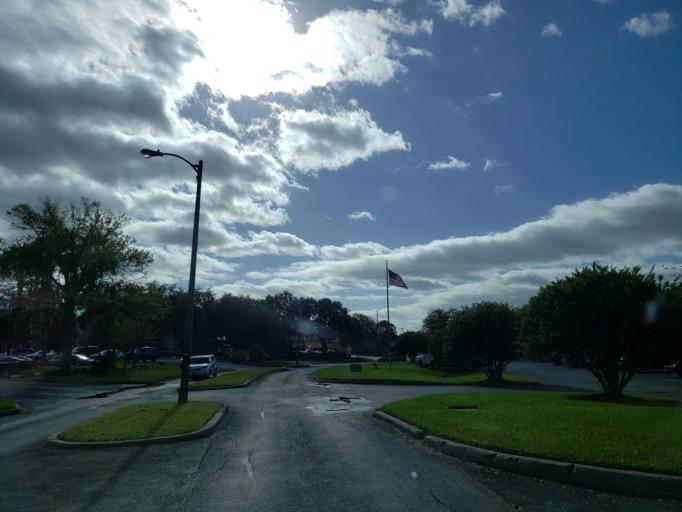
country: US
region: Florida
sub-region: Polk County
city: Medulla
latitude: 27.9735
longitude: -81.9637
